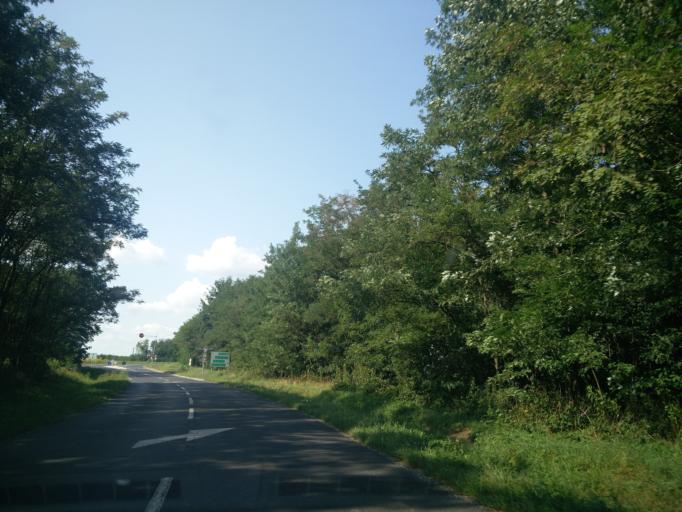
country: HU
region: Zala
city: Zalaegerszeg
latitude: 46.8720
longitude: 16.8033
